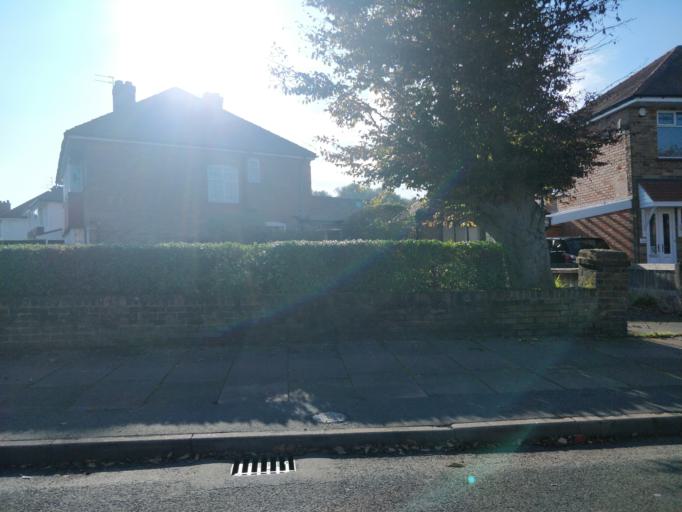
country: GB
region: England
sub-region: Lancashire
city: Banks
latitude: 53.6697
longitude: -2.9561
